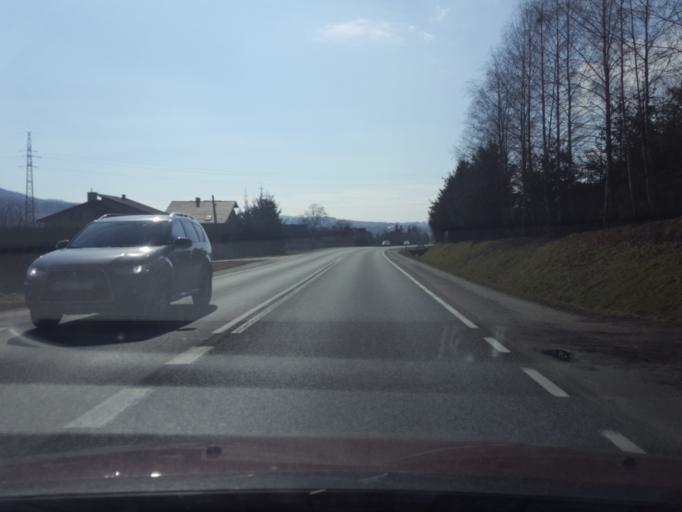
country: PL
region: Lesser Poland Voivodeship
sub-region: Powiat nowosadecki
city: Lososina Dolna
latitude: 49.7624
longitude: 20.6336
